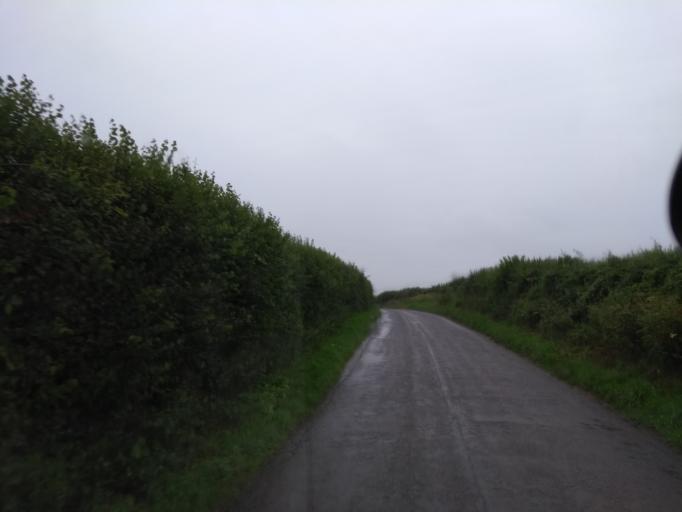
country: GB
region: England
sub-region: Somerset
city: Street
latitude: 51.0903
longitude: -2.6856
